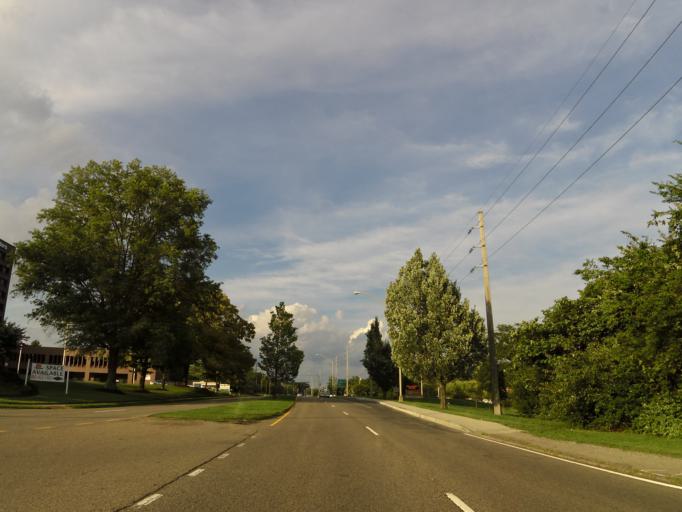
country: US
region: Tennessee
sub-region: Anderson County
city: Oak Ridge
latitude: 36.0266
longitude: -84.2379
